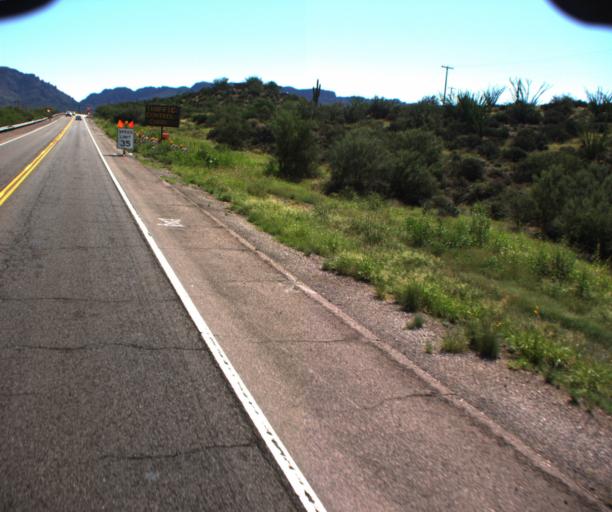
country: US
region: Arizona
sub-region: Pinal County
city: Superior
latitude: 33.2829
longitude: -111.1484
